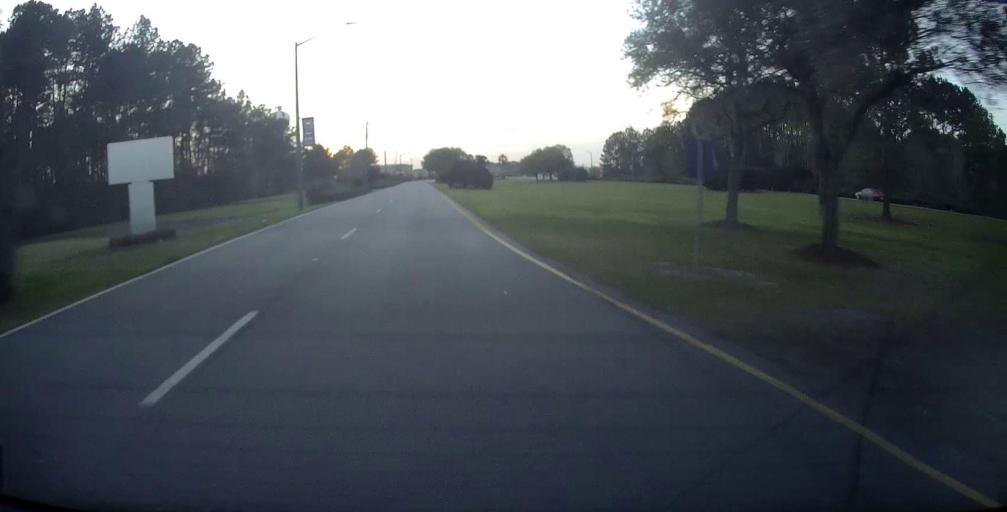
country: US
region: Georgia
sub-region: Chatham County
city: Pooler
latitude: 32.1378
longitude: -81.2276
